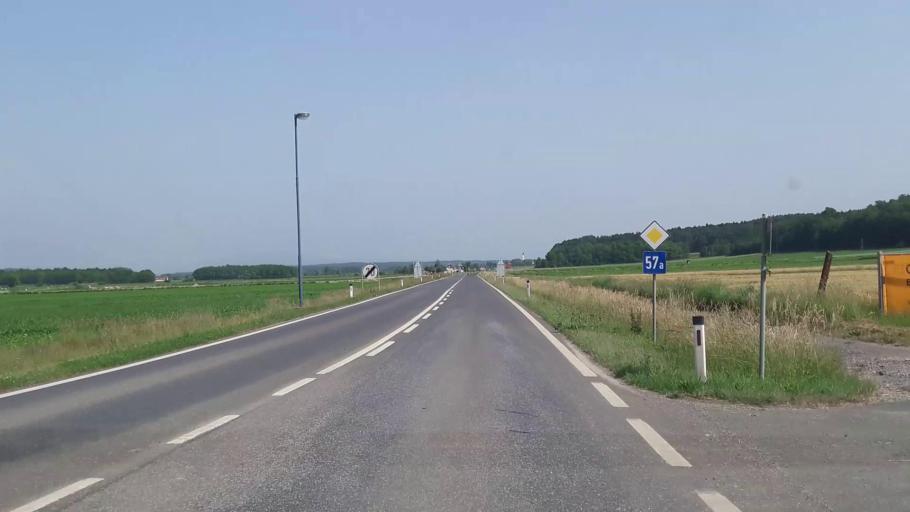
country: AT
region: Burgenland
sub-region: Politischer Bezirk Jennersdorf
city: Rudersdorf
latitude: 47.0601
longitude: 16.1168
